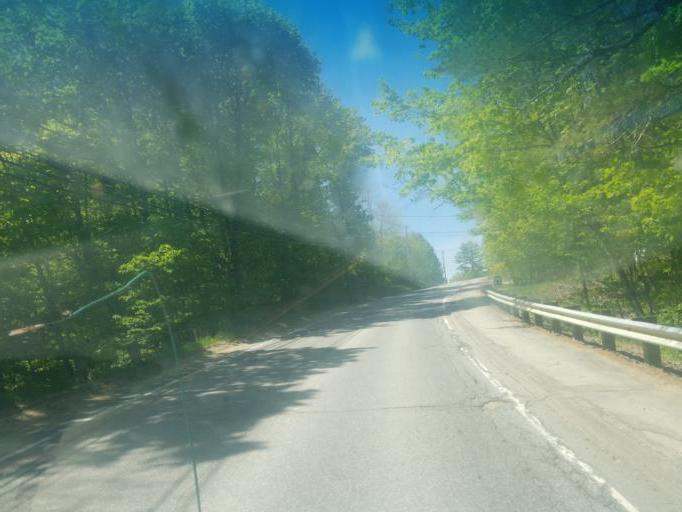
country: US
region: New Hampshire
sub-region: Grafton County
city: Plymouth
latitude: 43.7595
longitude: -71.7009
